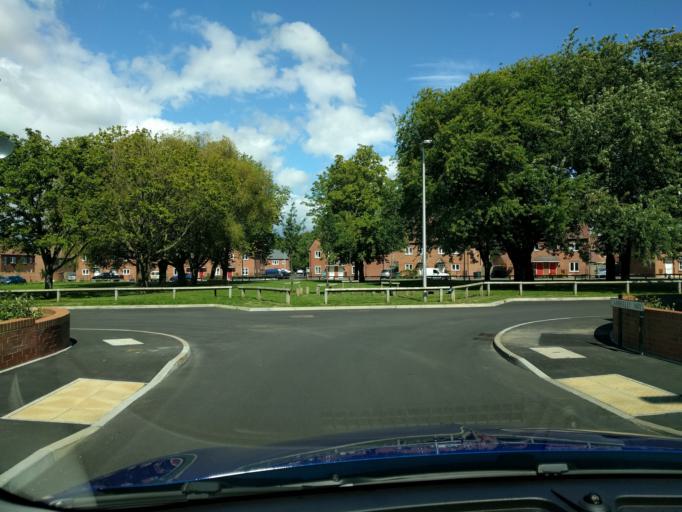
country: GB
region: England
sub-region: Gloucestershire
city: Mickleton
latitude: 52.1182
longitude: -1.7579
